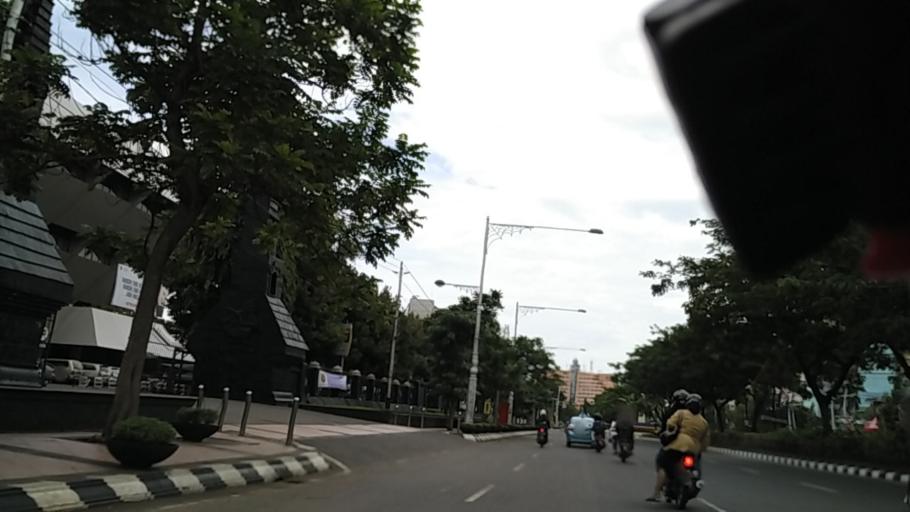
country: ID
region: Central Java
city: Semarang
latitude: -6.9944
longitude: 110.4207
